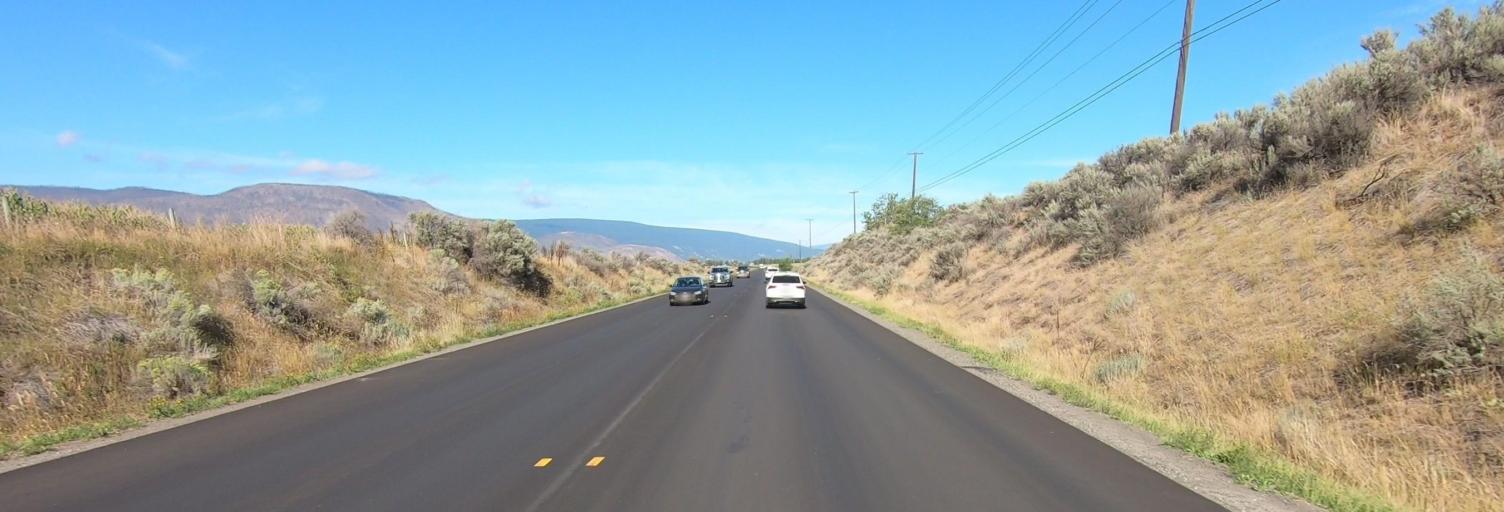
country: CA
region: British Columbia
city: Cache Creek
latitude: 50.7997
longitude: -121.2629
